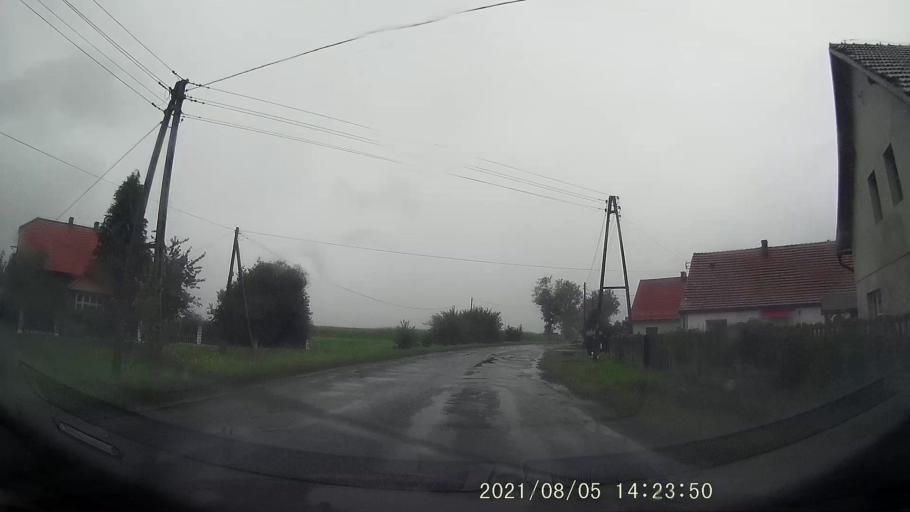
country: PL
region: Opole Voivodeship
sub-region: Powiat nyski
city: Korfantow
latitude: 50.4826
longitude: 17.6437
